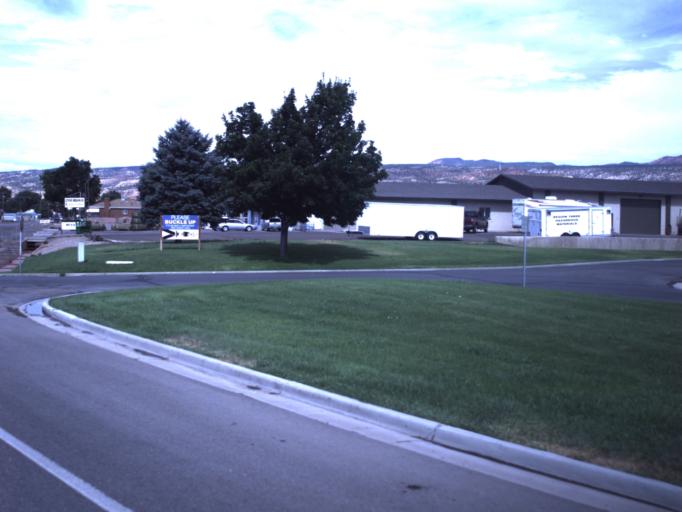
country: US
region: Utah
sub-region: Sevier County
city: Richfield
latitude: 38.7726
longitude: -112.0691
